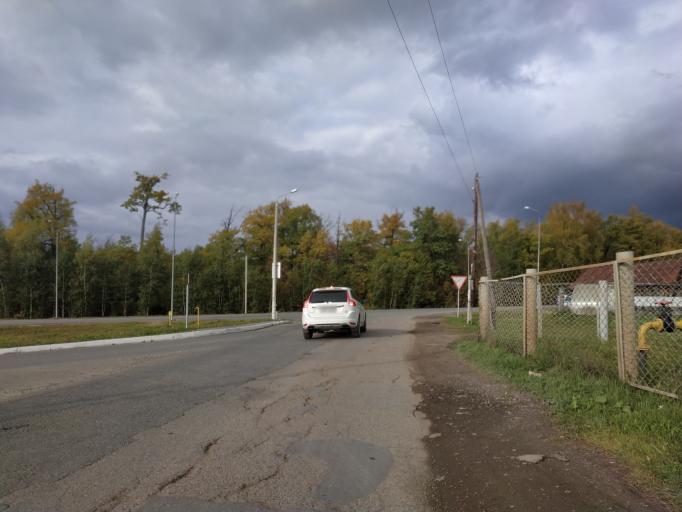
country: RU
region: Chuvashia
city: Ishley
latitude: 56.1333
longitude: 47.0867
